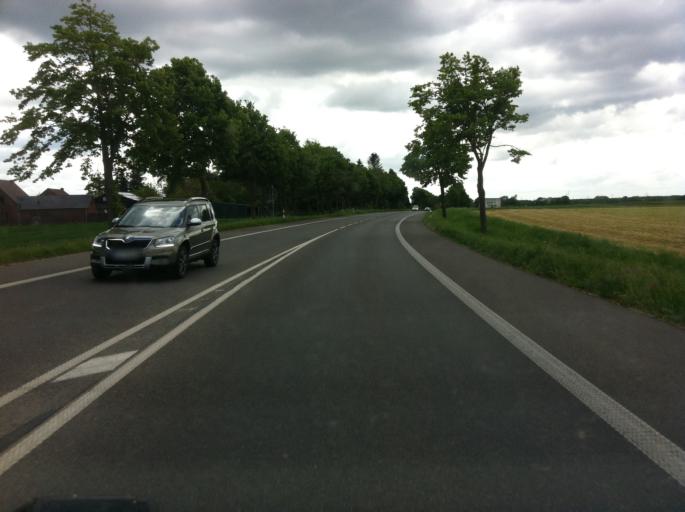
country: DE
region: North Rhine-Westphalia
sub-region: Regierungsbezirk Dusseldorf
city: Niederkruchten
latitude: 51.2198
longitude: 6.2071
